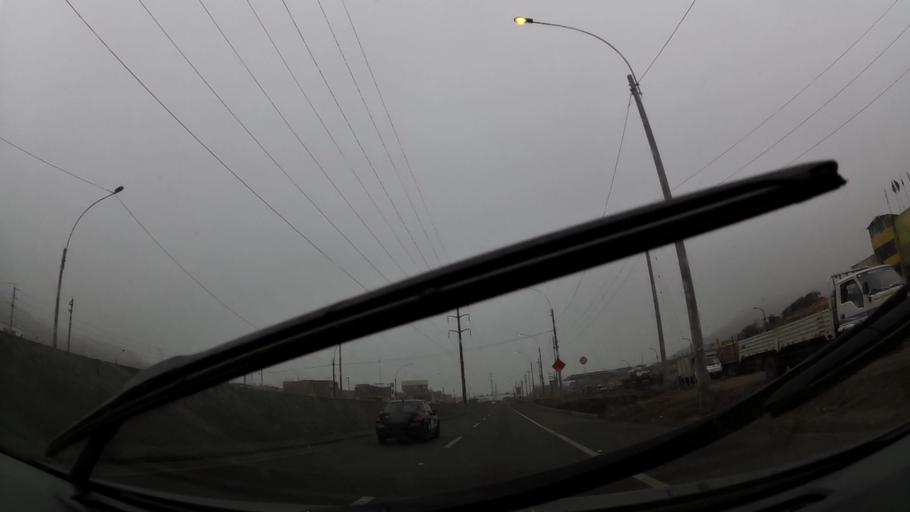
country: PE
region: Lima
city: Ventanilla
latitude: -11.8314
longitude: -77.1161
